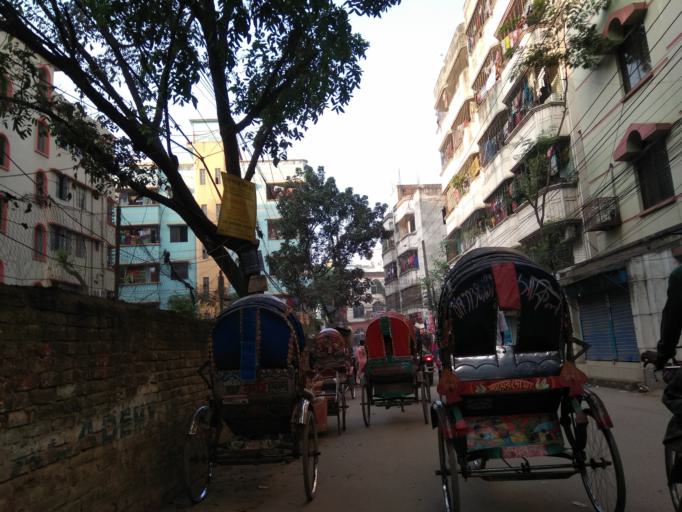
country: BD
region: Dhaka
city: Azimpur
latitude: 23.7598
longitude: 90.3571
